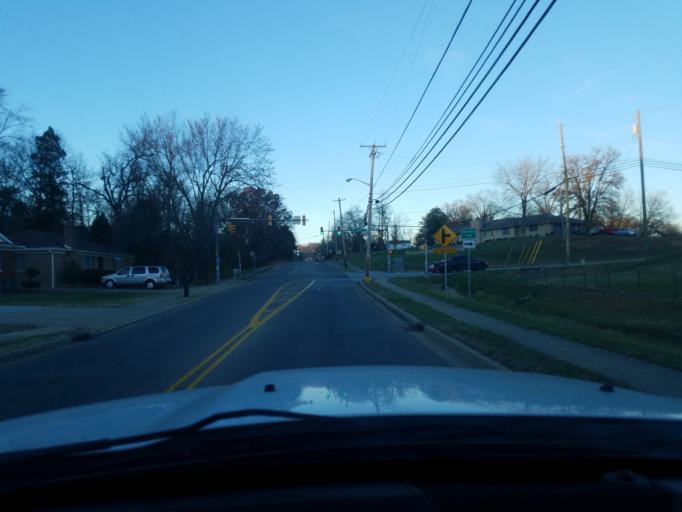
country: US
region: Indiana
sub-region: Floyd County
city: New Albany
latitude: 38.3314
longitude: -85.8365
